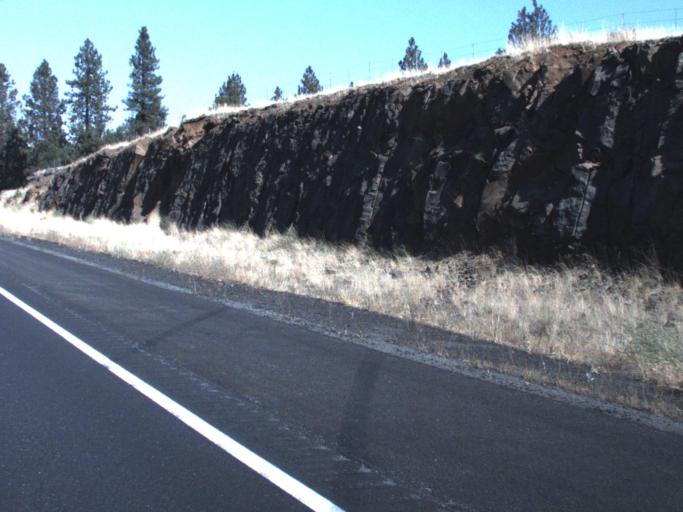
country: US
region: Washington
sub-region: Spokane County
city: Medical Lake
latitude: 47.4569
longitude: -117.7601
